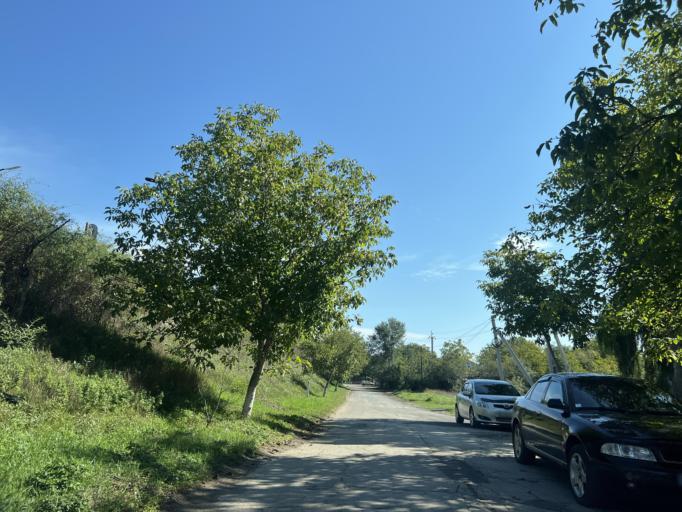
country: RO
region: Iasi
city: Ungheni-Prut
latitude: 47.1992
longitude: 27.7896
